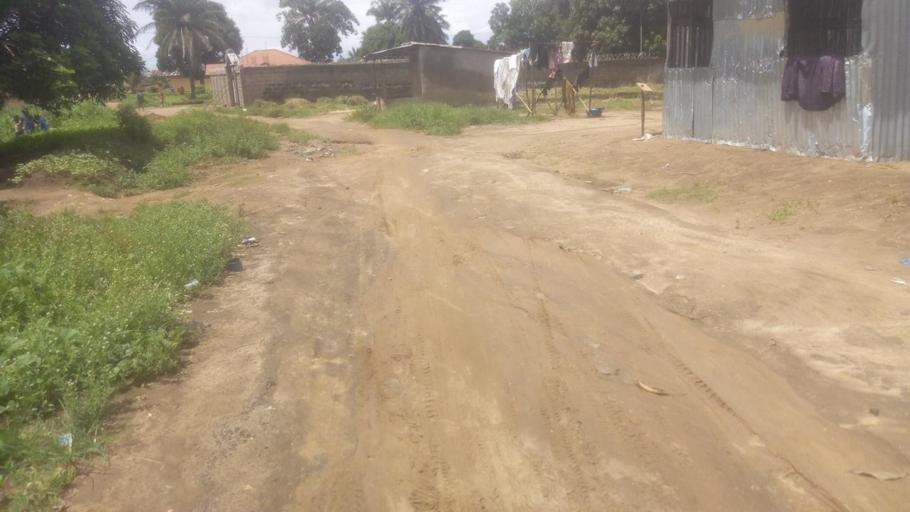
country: SL
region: Northern Province
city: Masoyila
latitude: 8.5992
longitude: -13.1813
